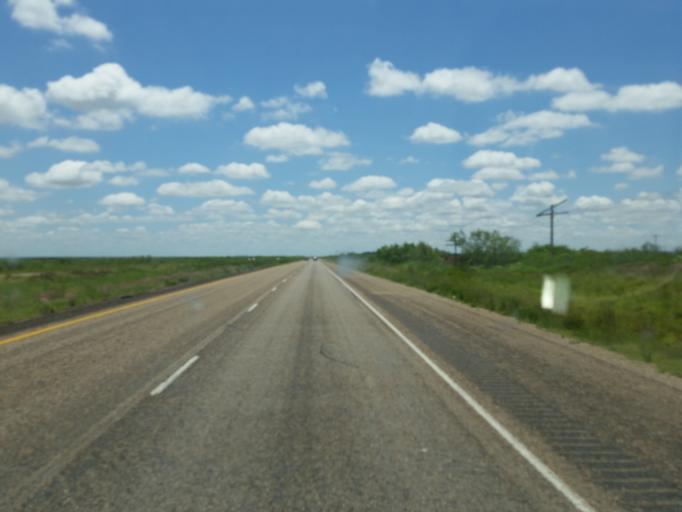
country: US
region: Texas
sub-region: Garza County
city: Post
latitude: 33.1303
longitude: -101.2995
